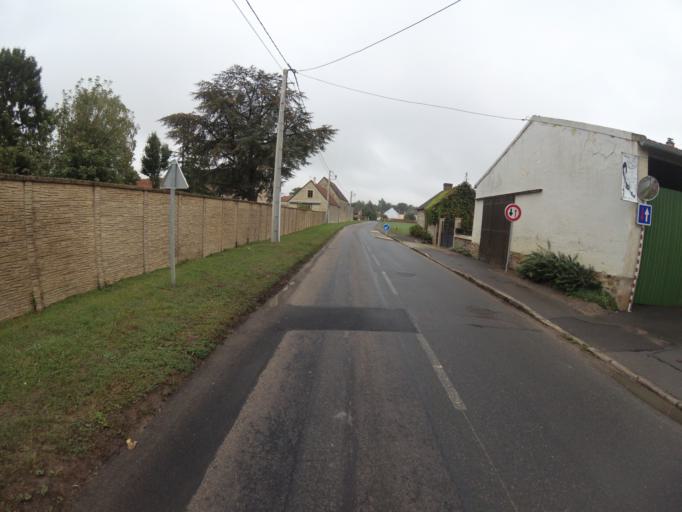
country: FR
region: Ile-de-France
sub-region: Departement de Seine-et-Marne
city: Chanteloup-en-Brie
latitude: 48.8416
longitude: 2.7516
